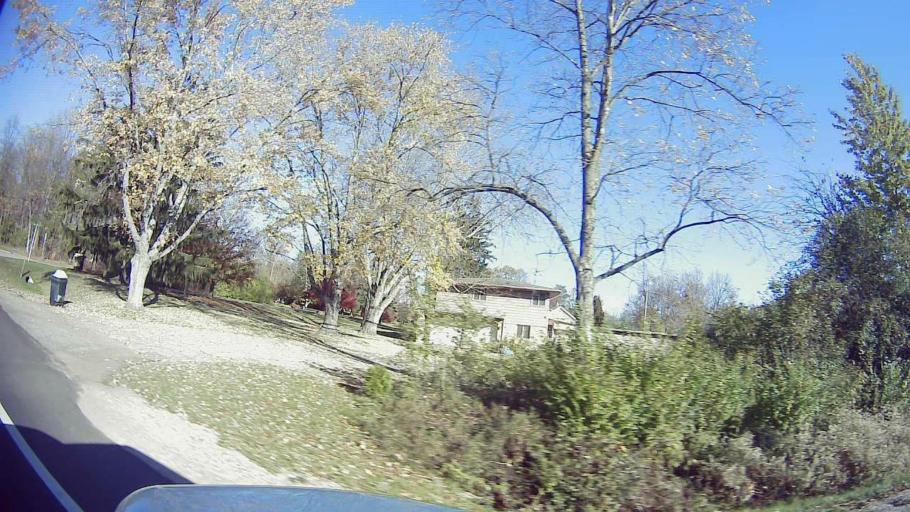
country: US
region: Michigan
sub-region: Oakland County
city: West Bloomfield Township
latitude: 42.5331
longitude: -83.3995
